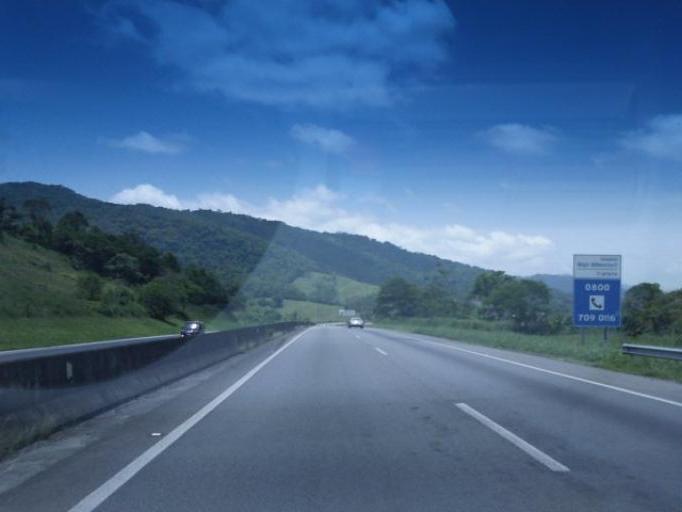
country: BR
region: Sao Paulo
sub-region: Miracatu
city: Miracatu
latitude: -24.2991
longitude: -47.4834
